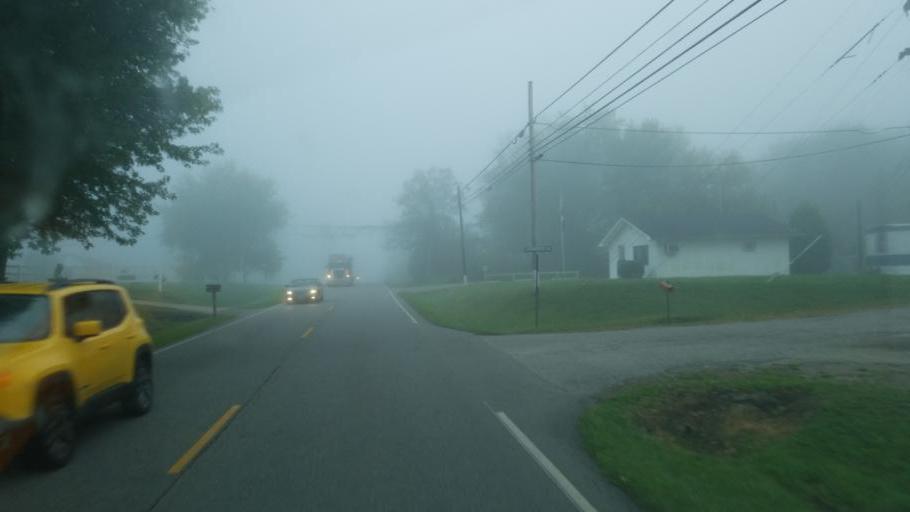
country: US
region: Ohio
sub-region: Scioto County
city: Portsmouth
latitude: 38.7088
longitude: -83.0281
